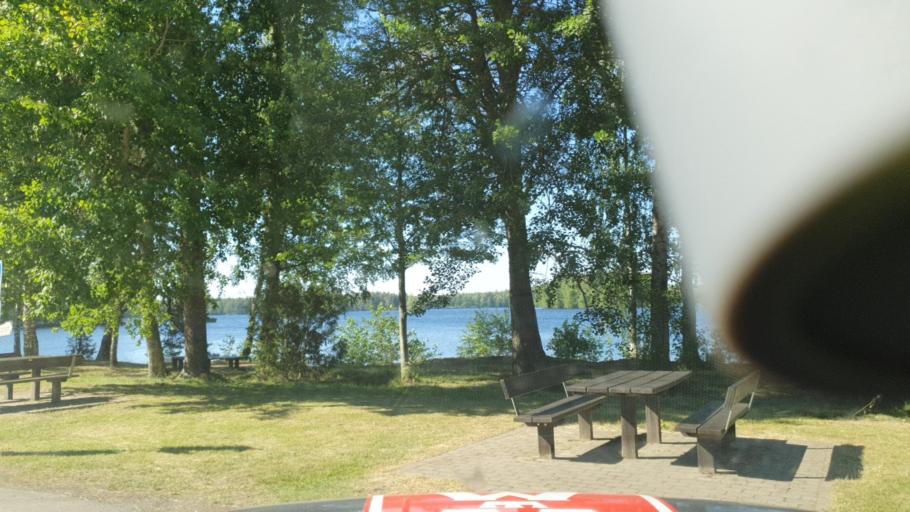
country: SE
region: Kalmar
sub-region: Nybro Kommun
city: Nybro
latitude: 56.8458
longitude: 15.7044
